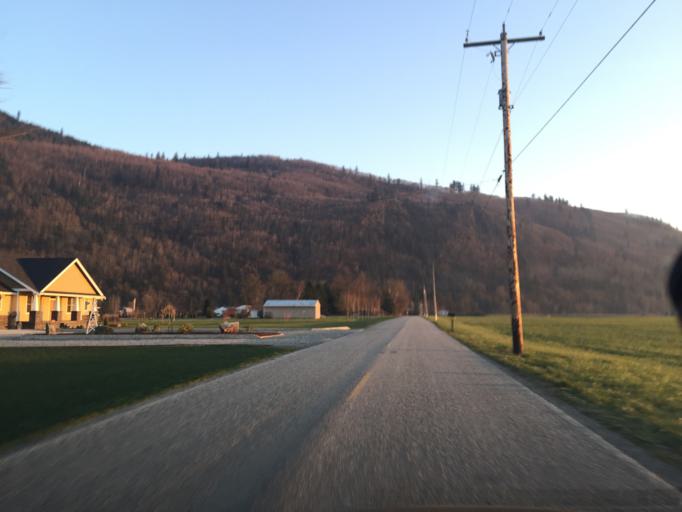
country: US
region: Washington
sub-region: Whatcom County
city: Peaceful Valley
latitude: 48.9972
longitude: -122.1839
